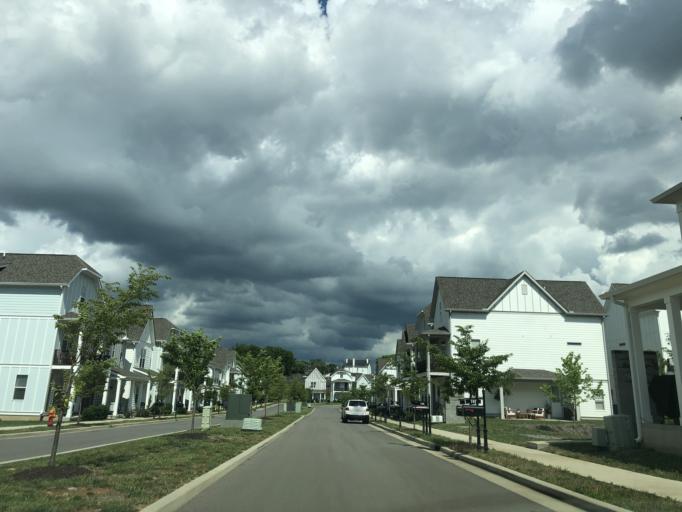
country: US
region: Tennessee
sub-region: Davidson County
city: Nashville
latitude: 36.2223
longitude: -86.7655
